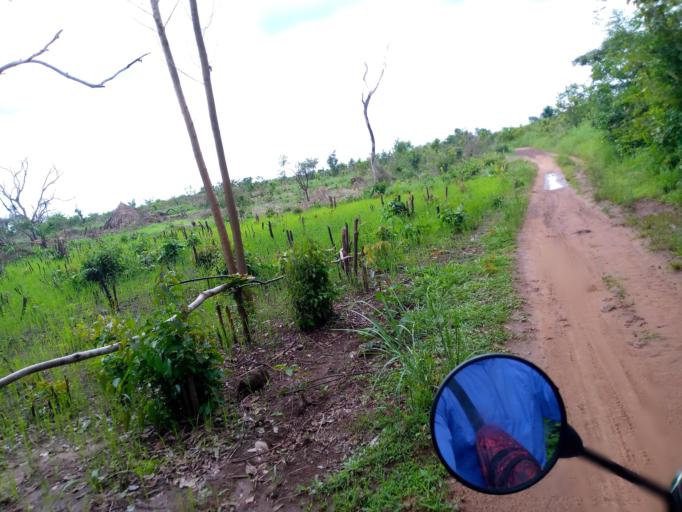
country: SL
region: Northern Province
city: Mange
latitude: 8.9830
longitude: -12.7310
